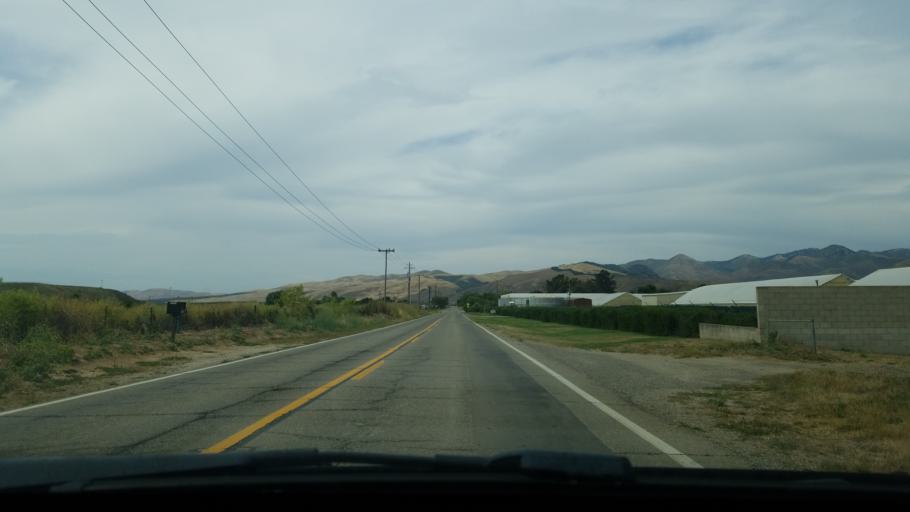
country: US
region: California
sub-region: Santa Barbara County
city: Orcutt
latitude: 34.8851
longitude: -120.3150
